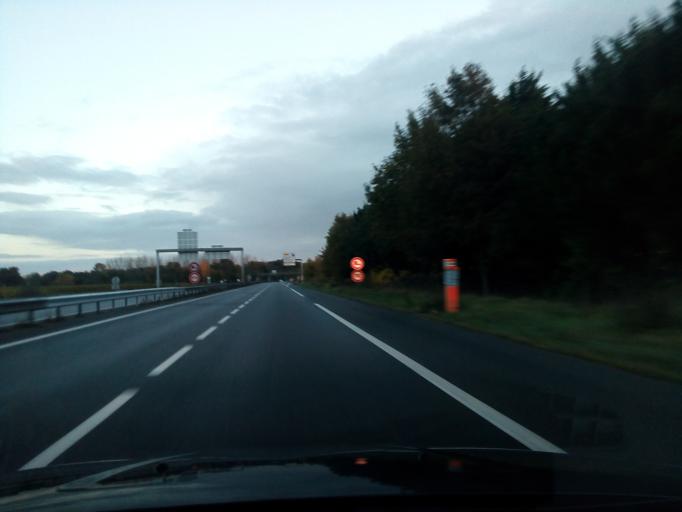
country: FR
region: Aquitaine
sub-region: Departement de la Gironde
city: Peujard
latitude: 45.0209
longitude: -0.4252
